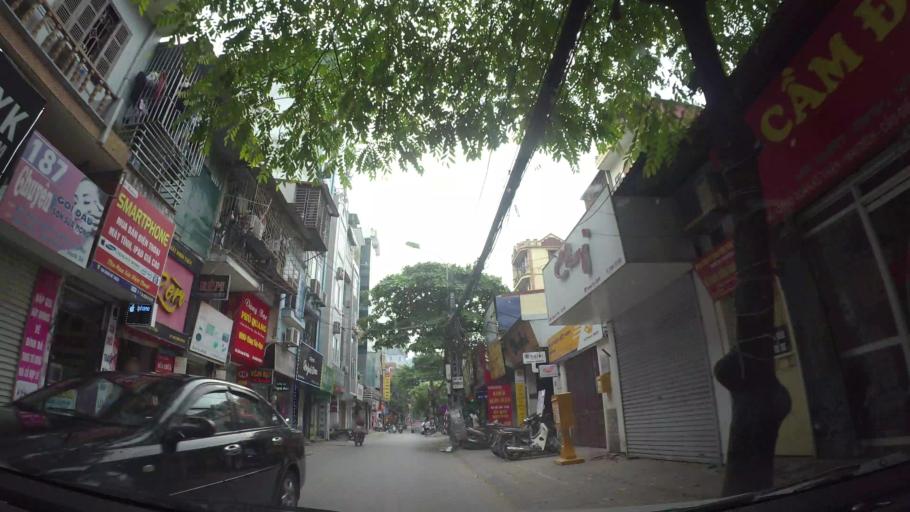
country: VN
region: Ha Noi
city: Cau Dien
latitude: 21.0417
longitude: 105.7764
